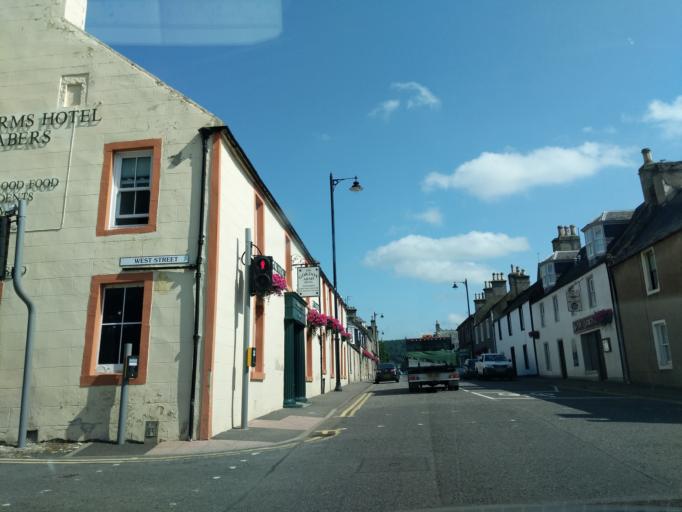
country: GB
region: Scotland
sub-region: Moray
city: Fochabers
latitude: 57.6150
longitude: -3.0998
